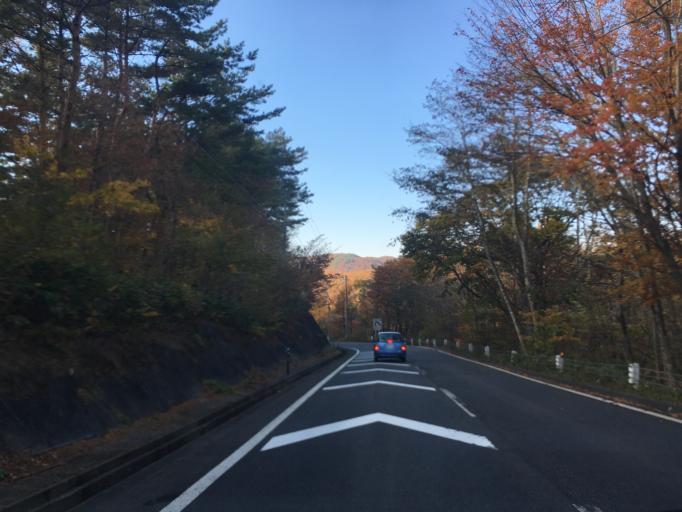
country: JP
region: Fukushima
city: Sukagawa
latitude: 37.2645
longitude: 140.0993
